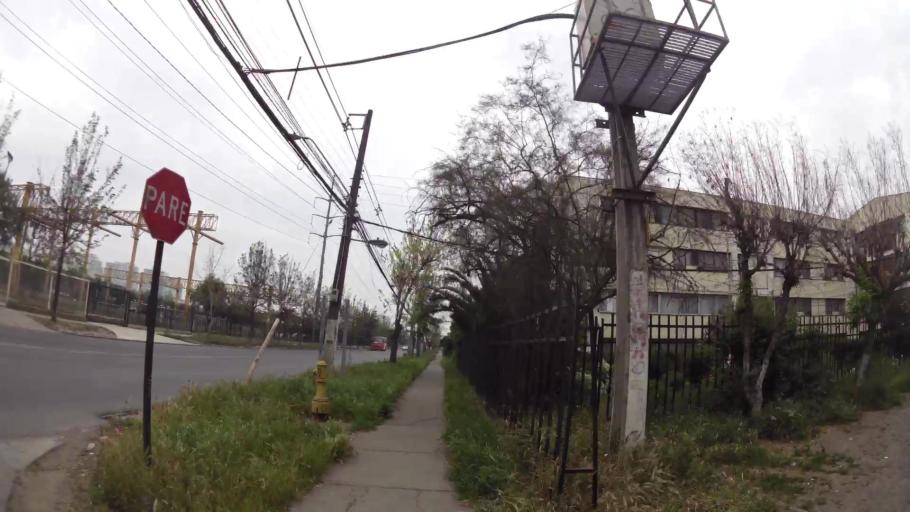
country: CL
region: Santiago Metropolitan
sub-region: Provincia de Santiago
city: Villa Presidente Frei, Nunoa, Santiago, Chile
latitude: -33.4852
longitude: -70.6105
